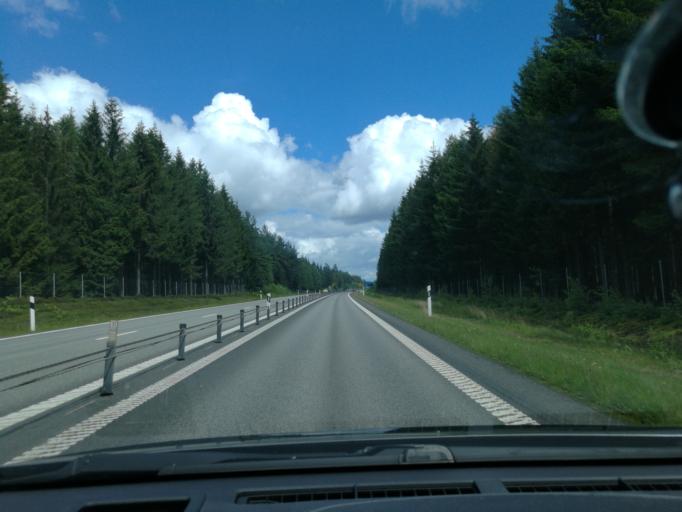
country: SE
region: Skane
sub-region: Hassleholms Kommun
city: Hassleholm
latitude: 56.1957
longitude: 13.8520
